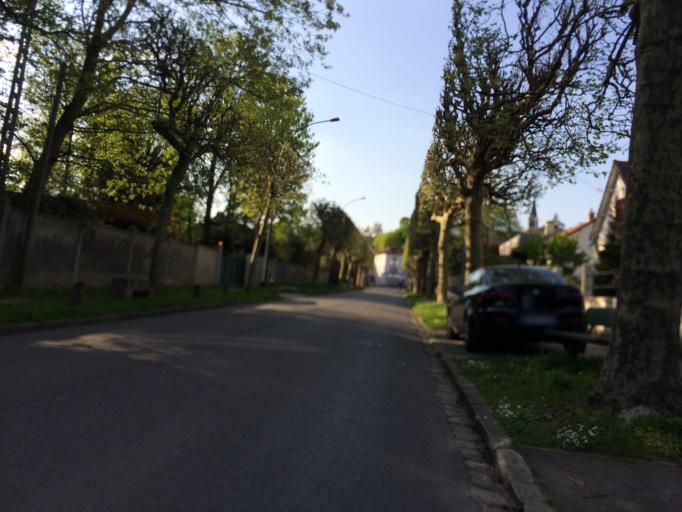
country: FR
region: Ile-de-France
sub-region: Departement de l'Essonne
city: Verrieres-le-Buisson
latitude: 48.7453
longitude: 2.2655
